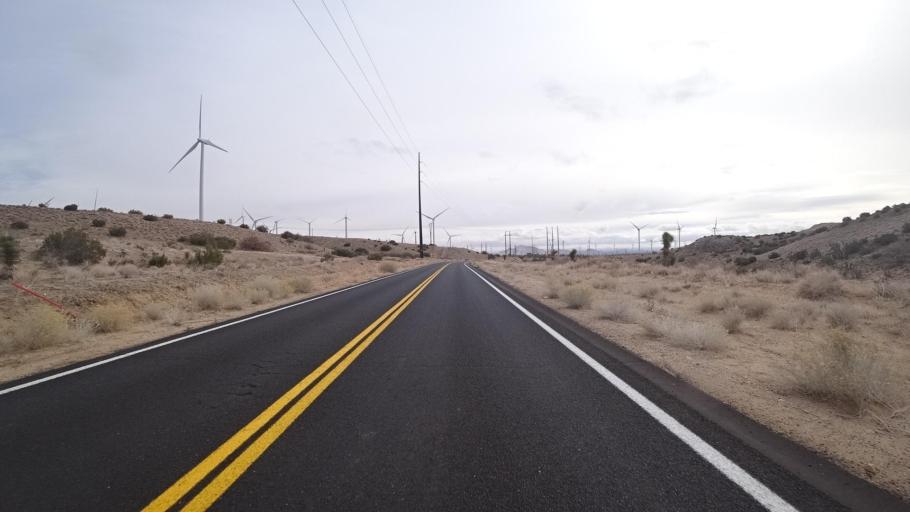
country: US
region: California
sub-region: Kern County
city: Mojave
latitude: 35.0463
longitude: -118.3161
